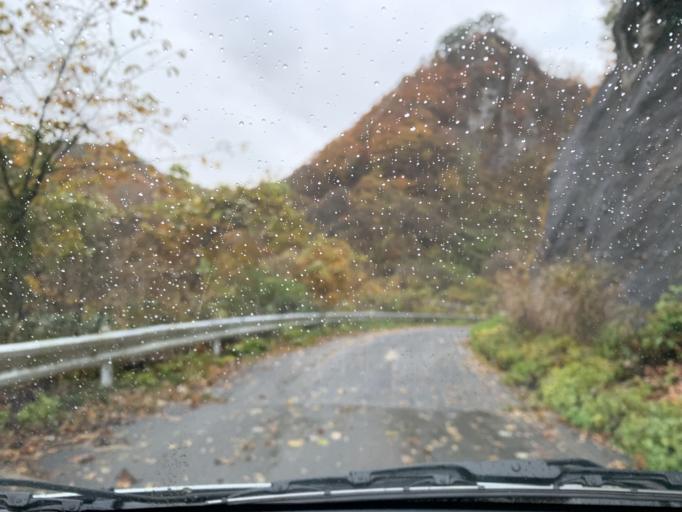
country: JP
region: Iwate
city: Mizusawa
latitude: 39.1014
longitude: 140.9397
